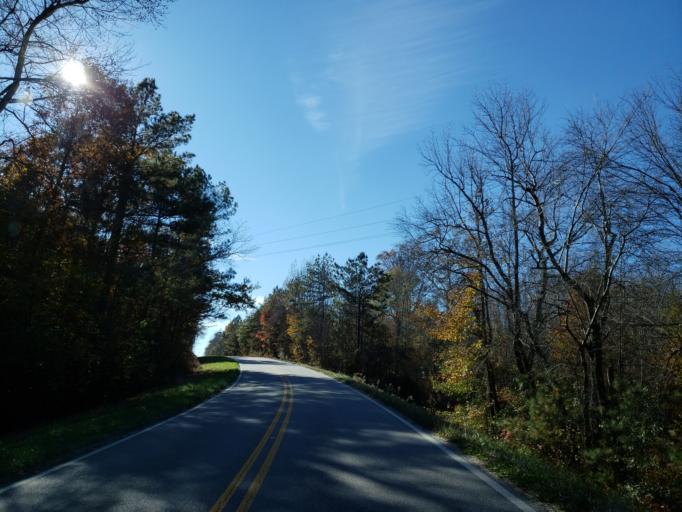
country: US
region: Alabama
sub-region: Cleburne County
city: Heflin
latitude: 33.6034
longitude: -85.6111
